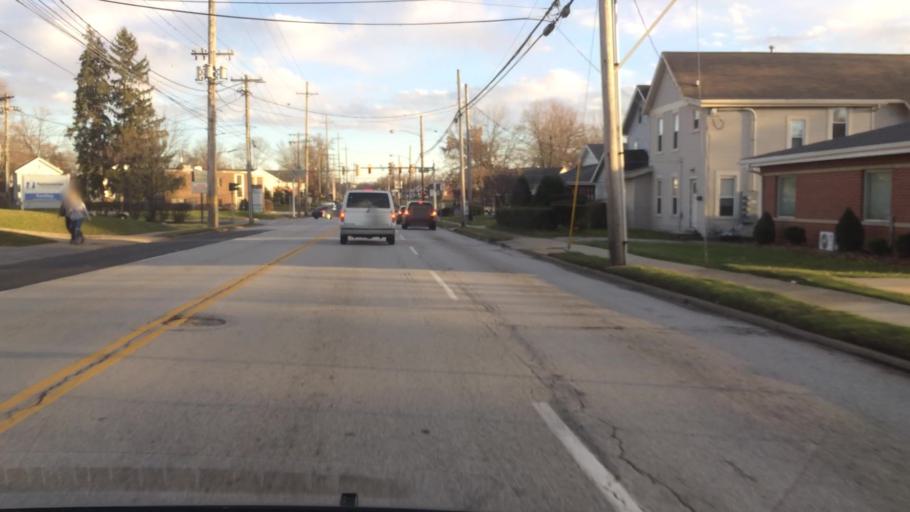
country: US
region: Ohio
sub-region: Summit County
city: Cuyahoga Falls
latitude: 41.1392
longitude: -81.4912
